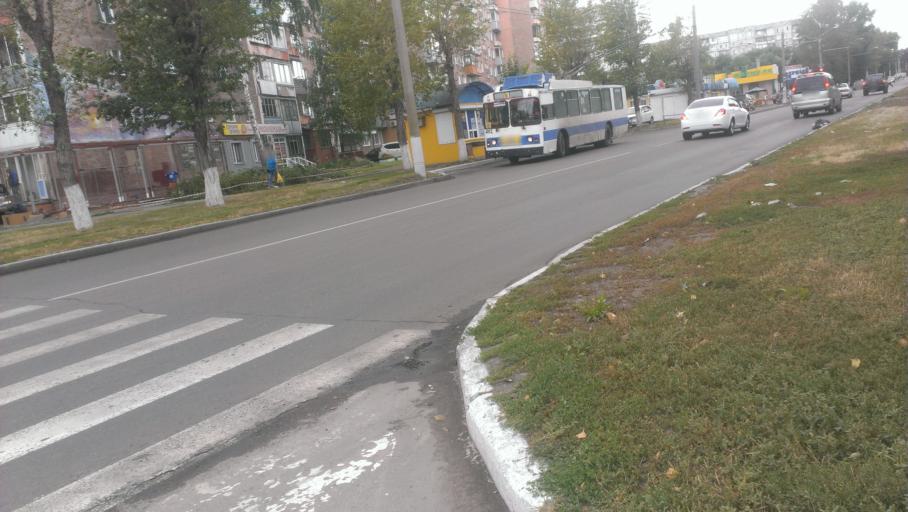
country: RU
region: Altai Krai
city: Novosilikatnyy
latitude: 53.3733
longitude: 83.6698
